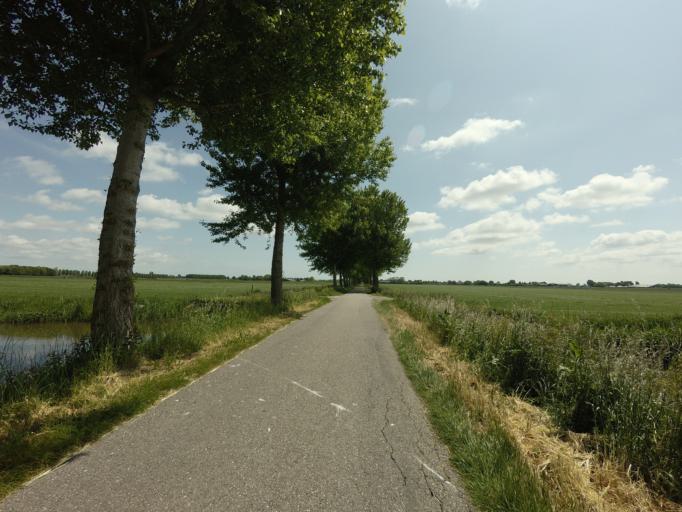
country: NL
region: North Holland
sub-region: Gemeente Beemster
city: Halfweg
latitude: 52.5986
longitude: 4.9284
